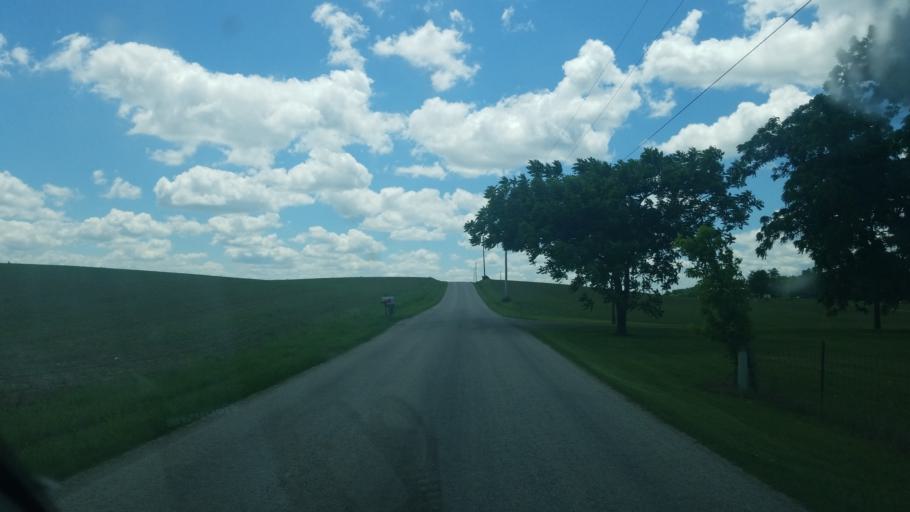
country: US
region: Ohio
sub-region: Huron County
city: New London
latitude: 40.9961
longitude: -82.3253
